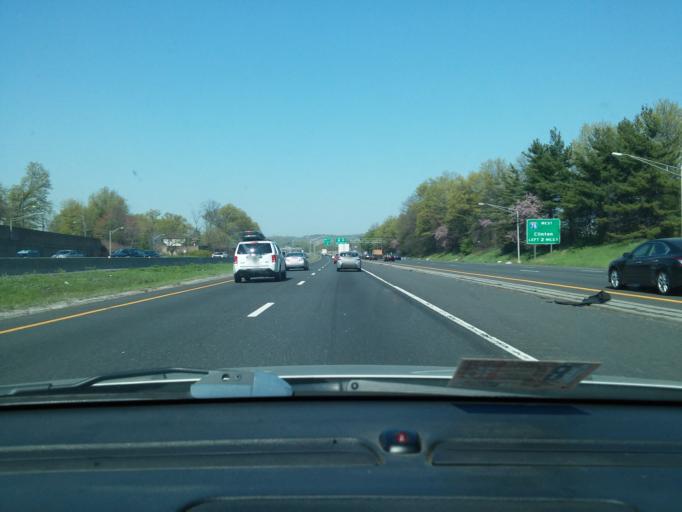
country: US
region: New Jersey
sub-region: Essex County
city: Maplewood
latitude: 40.7143
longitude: -74.2820
